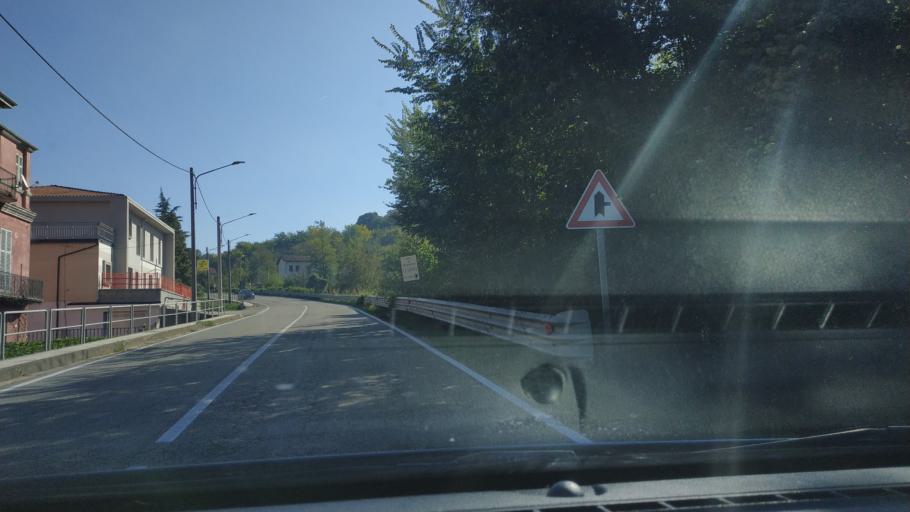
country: IT
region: Piedmont
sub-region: Provincia di Alessandria
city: Ozzano Monferrato
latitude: 45.1071
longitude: 8.3766
